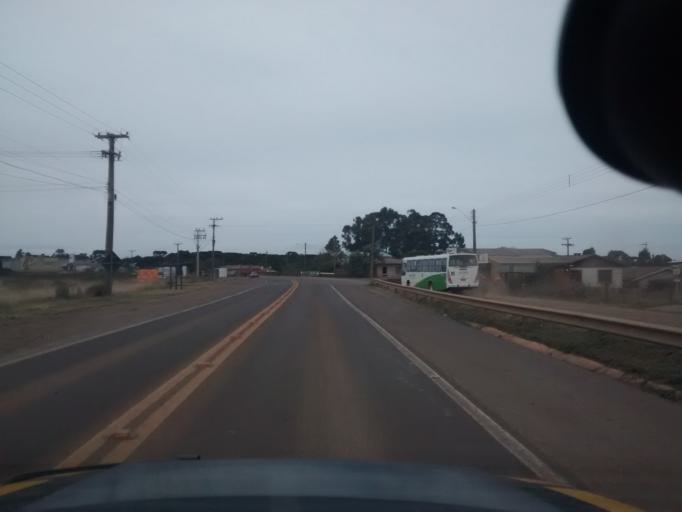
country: BR
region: Rio Grande do Sul
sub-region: Vacaria
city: Vacaria
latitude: -28.4864
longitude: -50.9598
